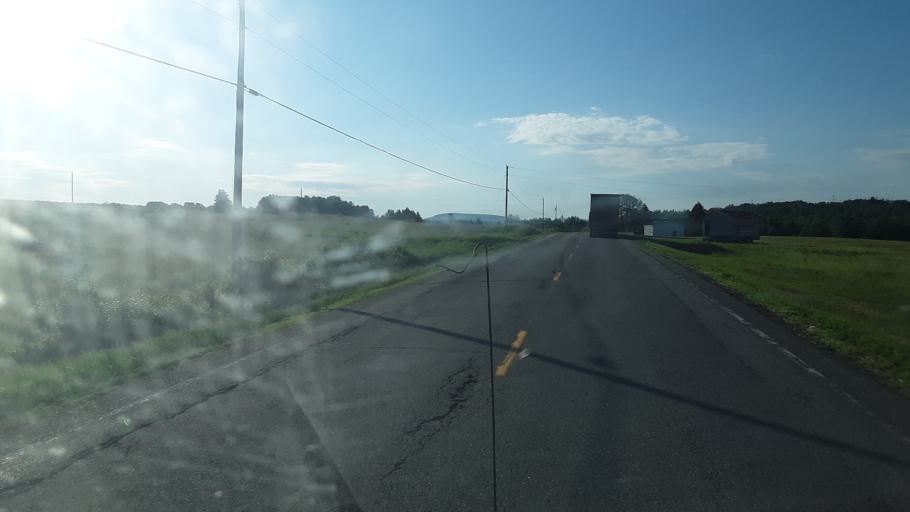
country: US
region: Maine
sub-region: Penobscot County
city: Patten
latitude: 46.1360
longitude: -68.1884
